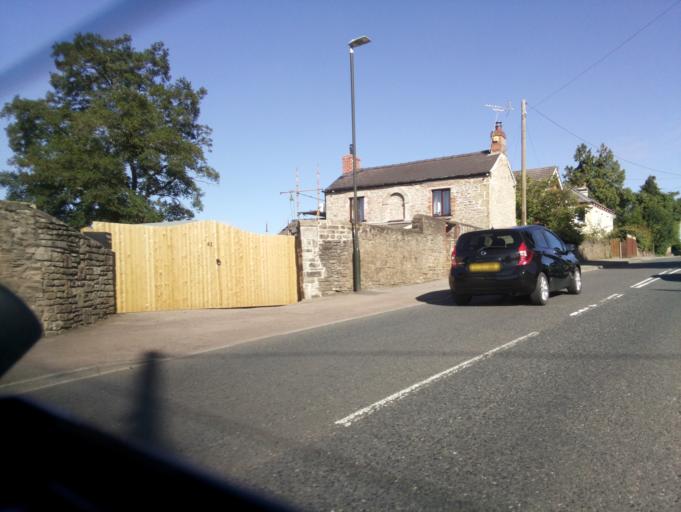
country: GB
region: England
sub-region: Gloucestershire
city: Coleford
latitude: 51.7968
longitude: -2.6205
